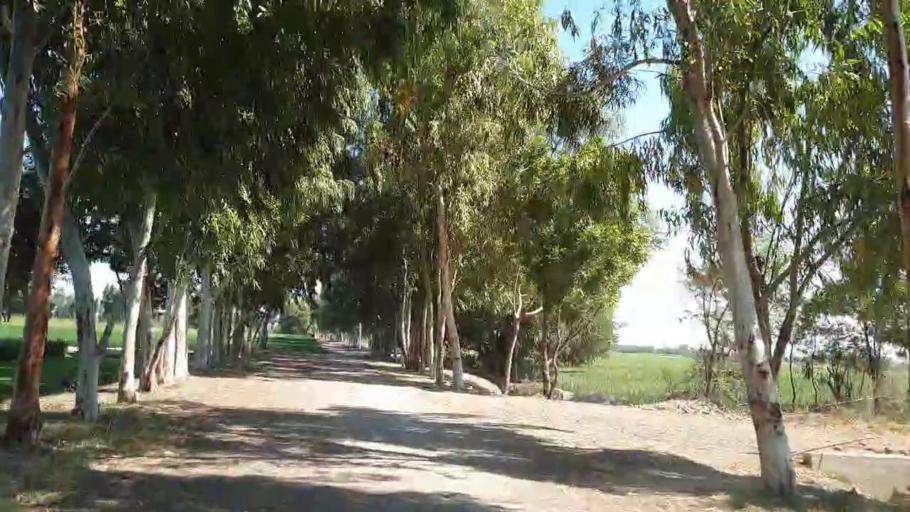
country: PK
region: Sindh
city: Pithoro
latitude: 25.6133
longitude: 69.2739
